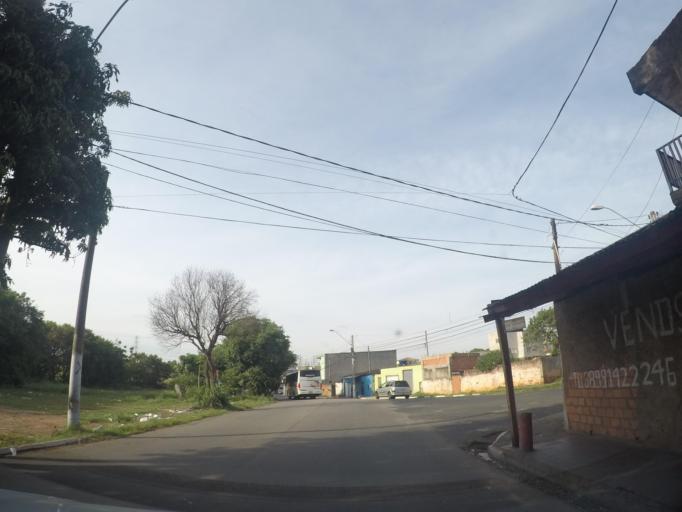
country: BR
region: Sao Paulo
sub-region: Hortolandia
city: Hortolandia
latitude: -22.8394
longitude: -47.1888
